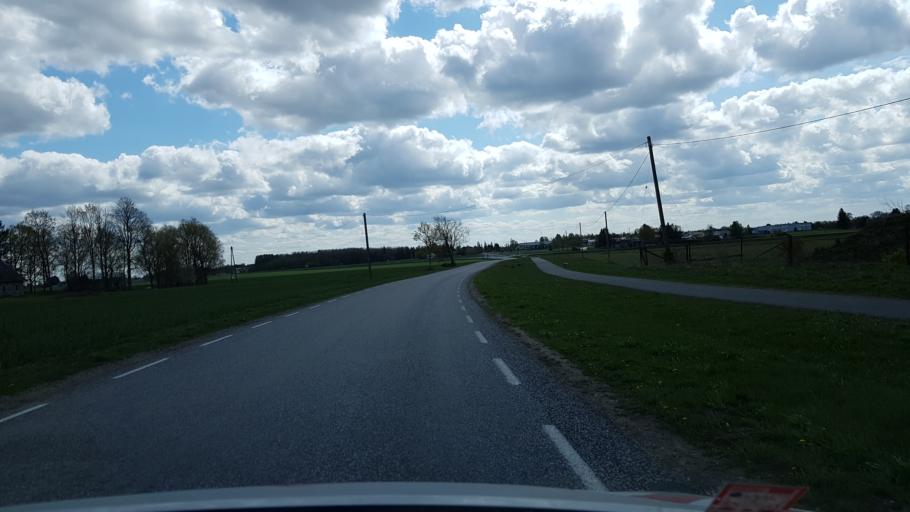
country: EE
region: Jogevamaa
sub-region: Poltsamaa linn
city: Poltsamaa
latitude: 58.6751
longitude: 25.9597
